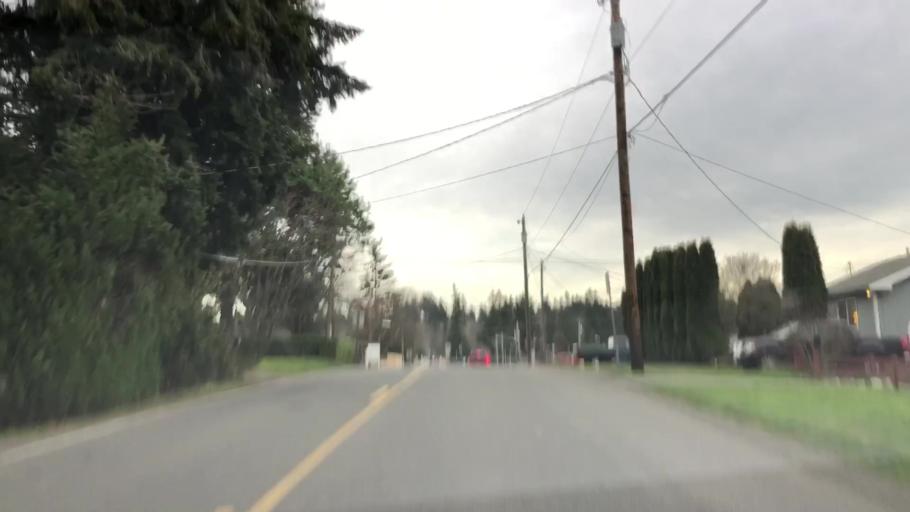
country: US
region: Washington
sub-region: Snohomish County
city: Esperance
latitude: 47.7960
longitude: -122.3369
